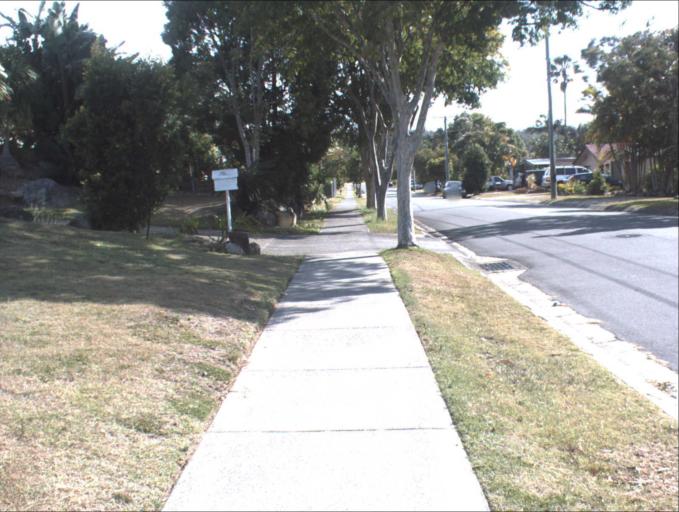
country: AU
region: Queensland
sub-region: Logan
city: Slacks Creek
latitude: -27.6587
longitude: 153.1812
